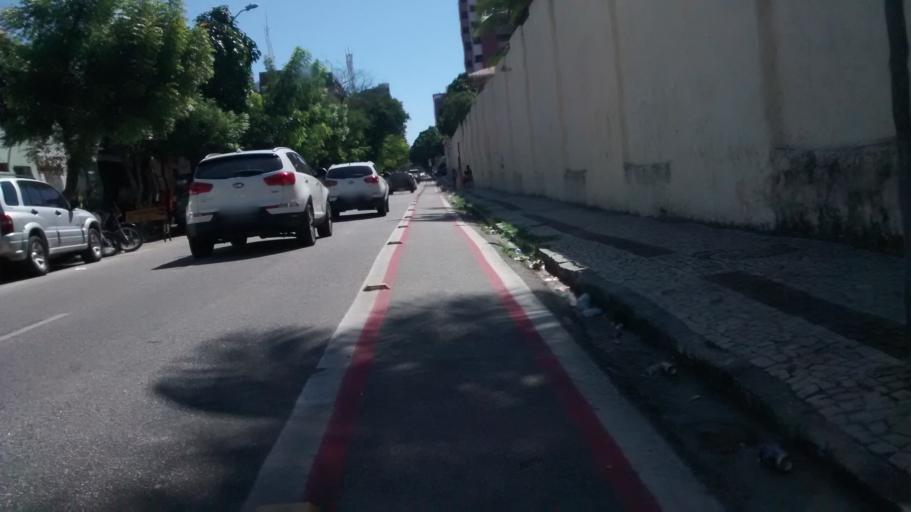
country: BR
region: Ceara
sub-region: Fortaleza
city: Fortaleza
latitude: -3.7445
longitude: -38.4964
